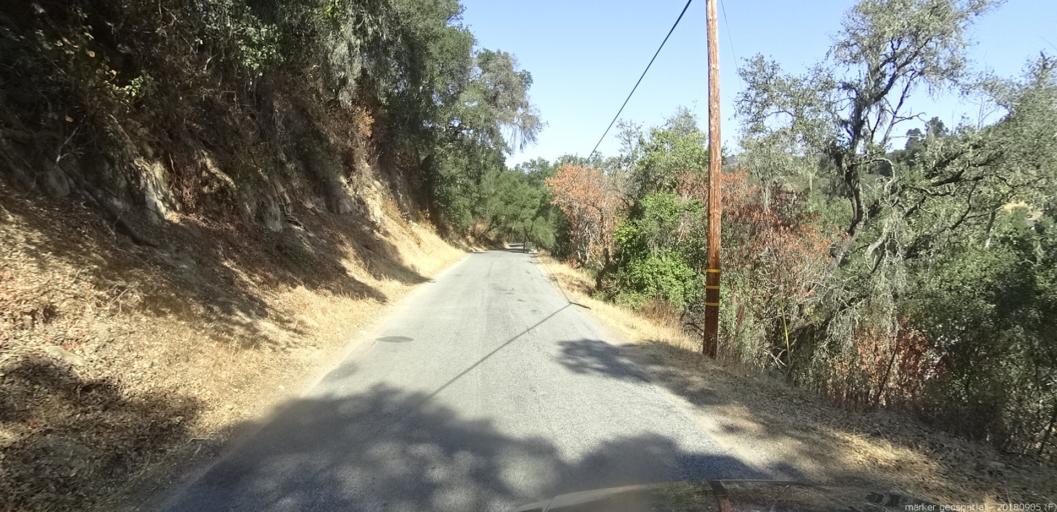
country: US
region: California
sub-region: Monterey County
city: Carmel Valley Village
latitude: 36.3940
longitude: -121.6407
